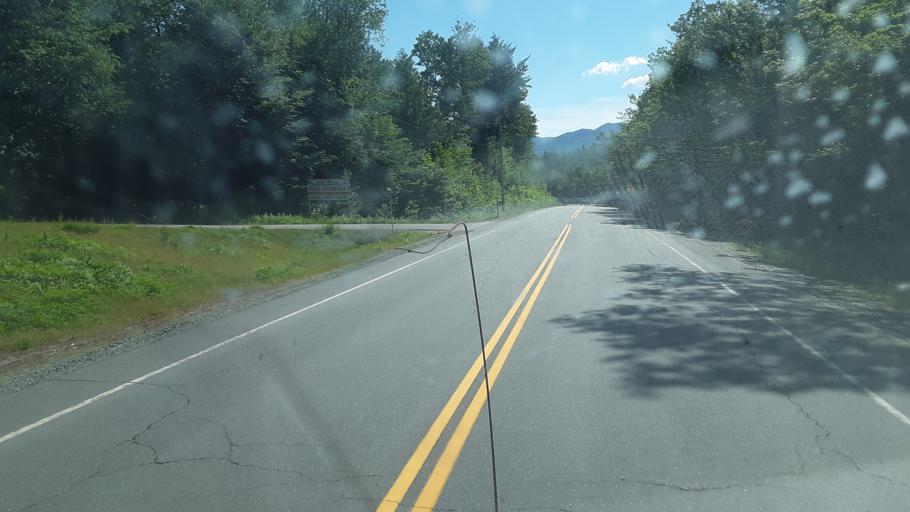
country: US
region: New Hampshire
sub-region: Grafton County
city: Woodstock
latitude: 44.0211
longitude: -71.7357
